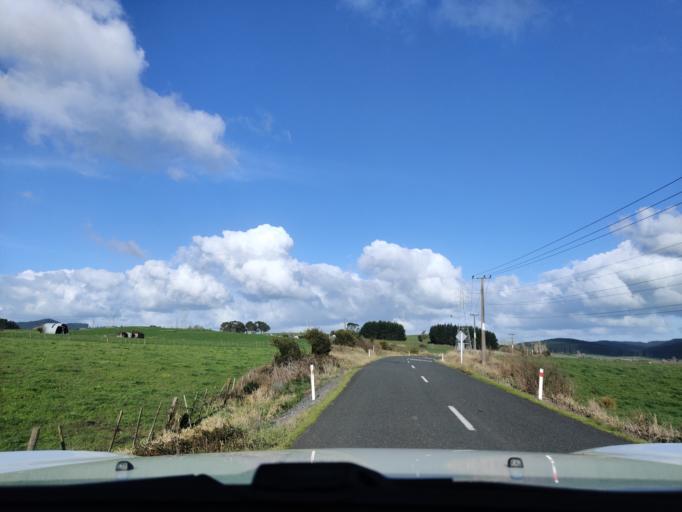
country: NZ
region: Waikato
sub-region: Waikato District
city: Te Kauwhata
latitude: -37.2634
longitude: 175.1959
